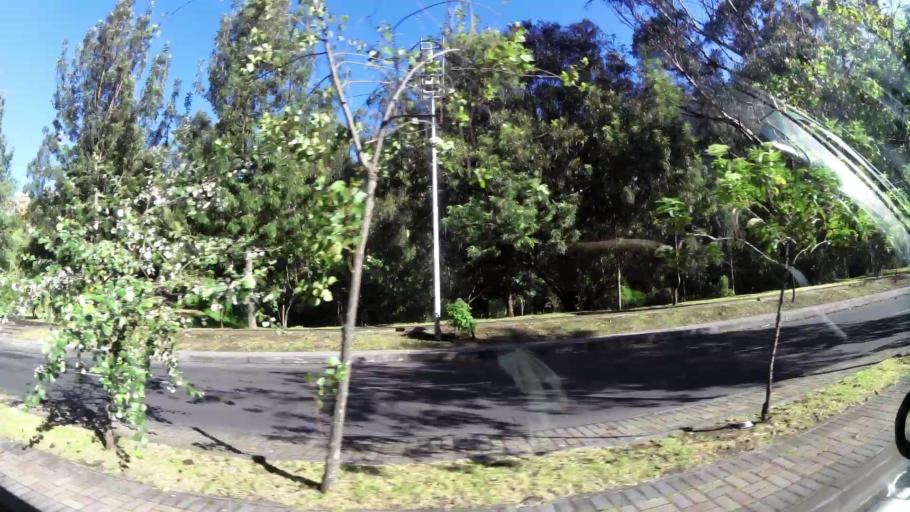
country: EC
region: Pichincha
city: Quito
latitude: -0.2362
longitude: -78.5185
